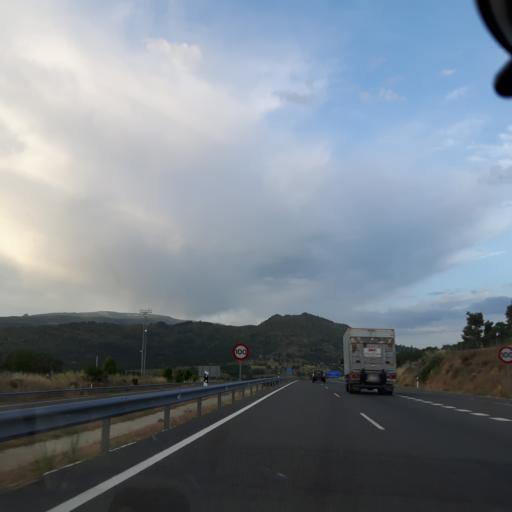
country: ES
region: Castille and Leon
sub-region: Provincia de Salamanca
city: Sorihuela
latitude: 40.4480
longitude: -5.6847
